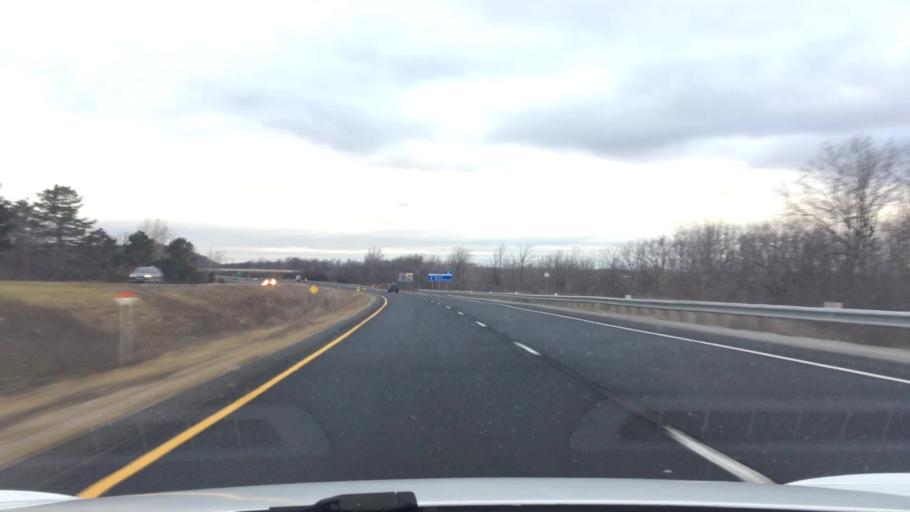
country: CA
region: Ontario
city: Niagara Falls
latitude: 43.1532
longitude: -79.1267
